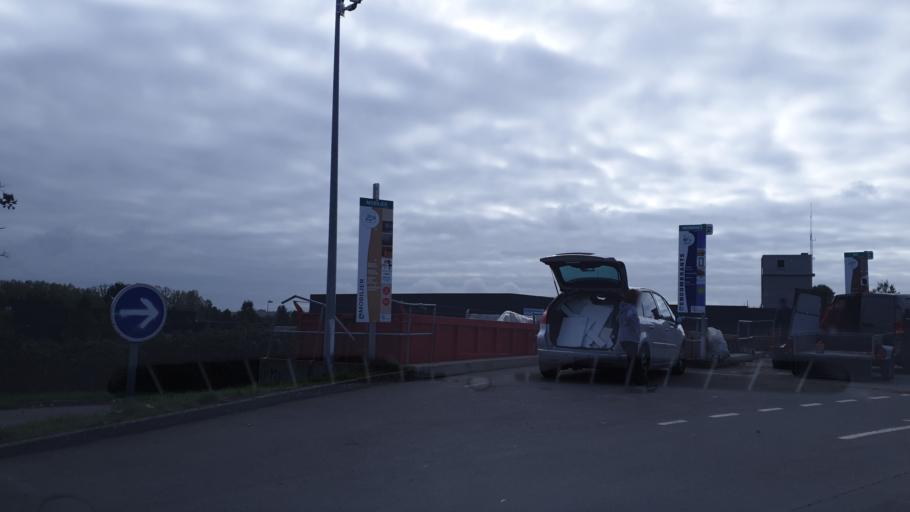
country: FR
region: Brittany
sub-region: Departement d'Ille-et-Vilaine
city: Janze
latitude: 47.9530
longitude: -1.4912
